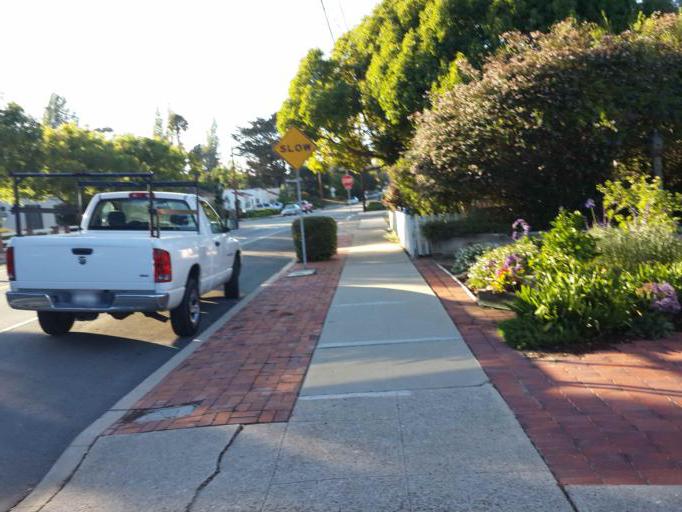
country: US
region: California
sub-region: San Luis Obispo County
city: San Luis Obispo
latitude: 35.2883
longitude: -120.6691
